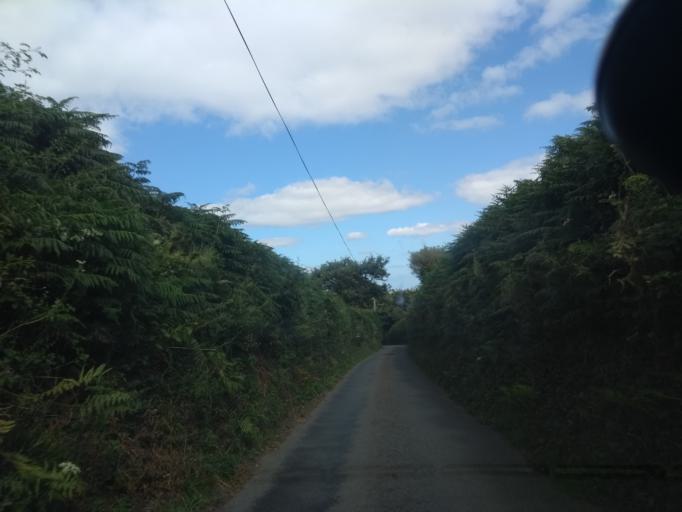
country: GB
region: England
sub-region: Devon
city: Modbury
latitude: 50.3064
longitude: -3.8636
